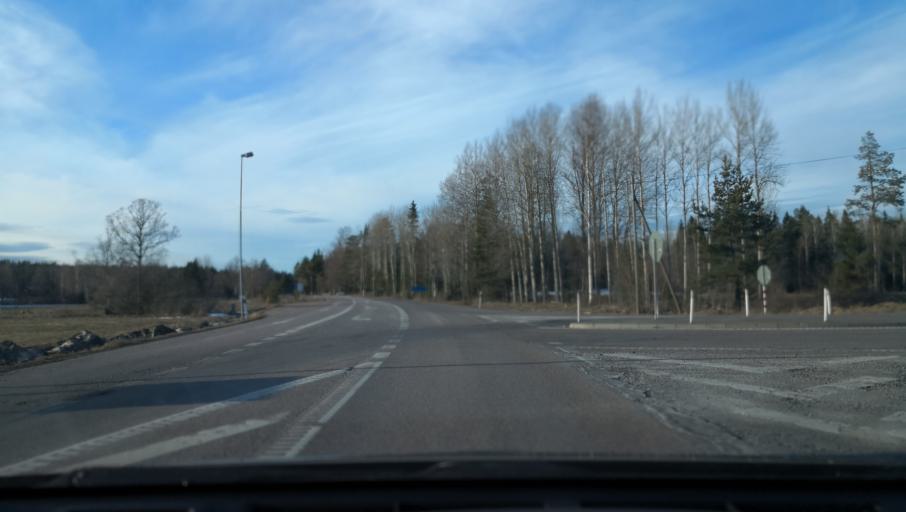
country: SE
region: Uppsala
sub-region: Osthammars Kommun
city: OEsthammar
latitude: 60.2977
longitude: 18.2828
